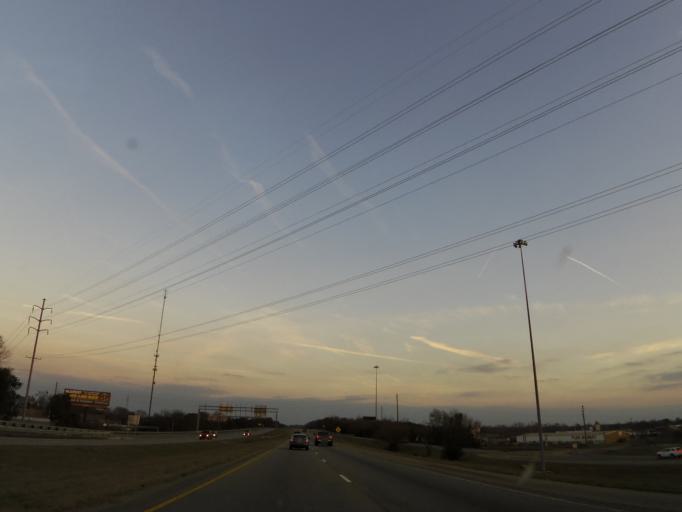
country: US
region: Georgia
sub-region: Dougherty County
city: Albany
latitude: 31.6056
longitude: -84.1534
